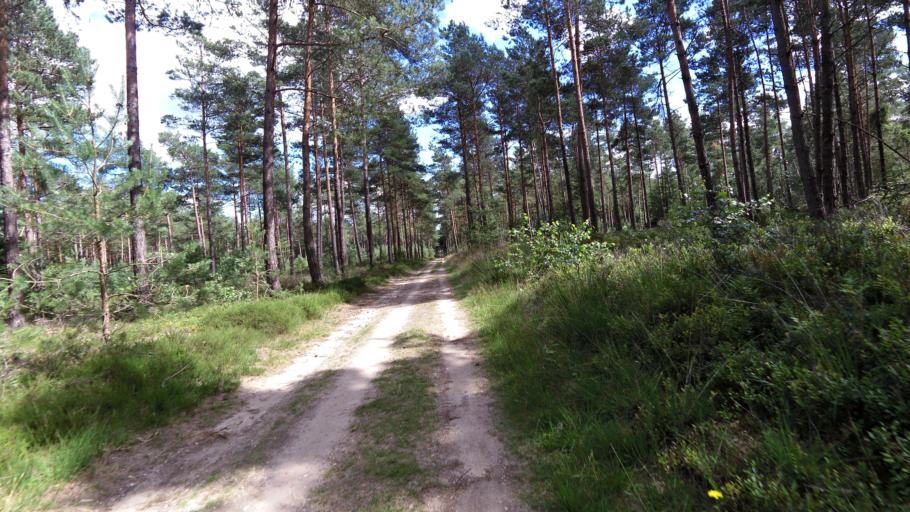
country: NL
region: Gelderland
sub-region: Gemeente Epe
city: Vaassen
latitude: 52.2546
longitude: 5.9099
